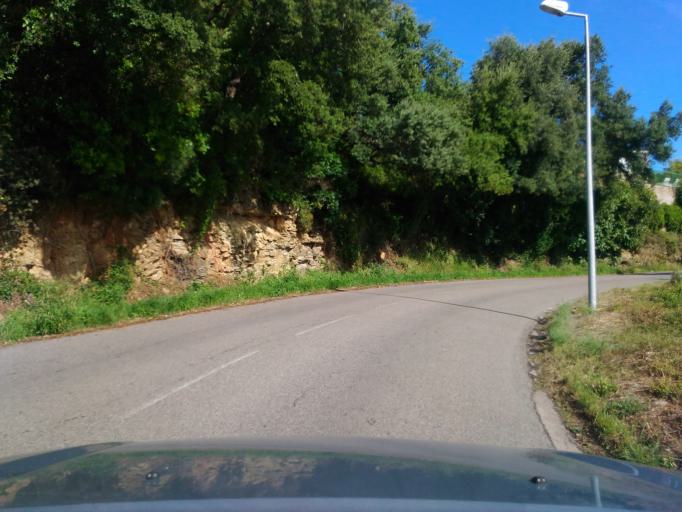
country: FR
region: Corsica
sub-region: Departement de la Haute-Corse
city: Brando
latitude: 42.7848
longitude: 9.4825
